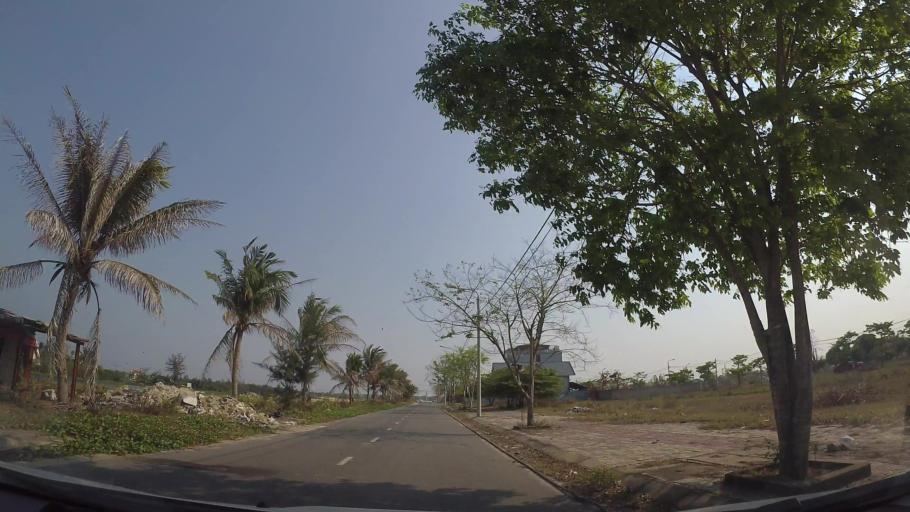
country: VN
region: Da Nang
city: Ngu Hanh Son
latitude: 15.9565
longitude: 108.2828
